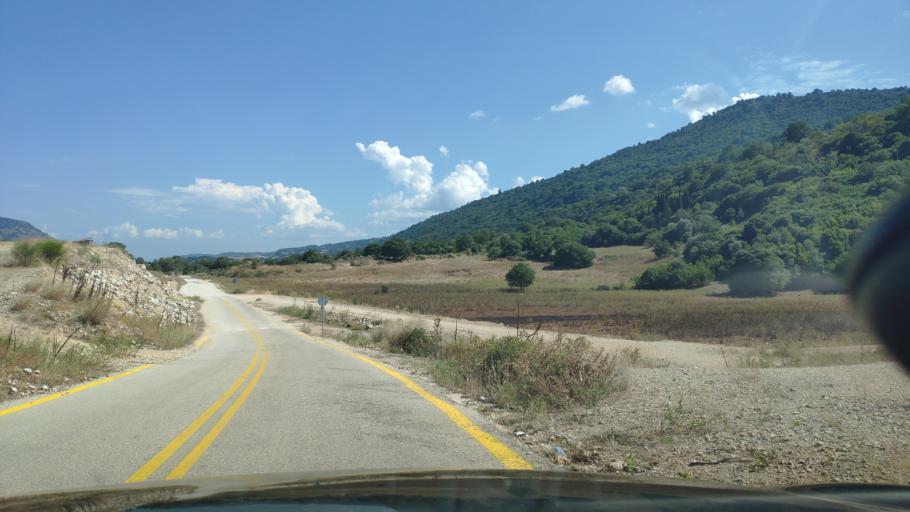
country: GR
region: West Greece
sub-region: Nomos Aitolias kai Akarnanias
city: Katouna
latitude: 38.8533
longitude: 21.0890
